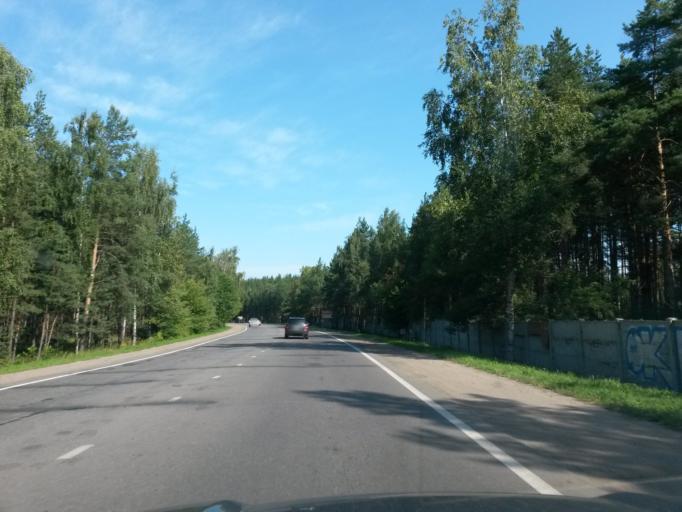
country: RU
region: Jaroslavl
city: Yaroslavl
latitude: 57.6719
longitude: 39.9085
